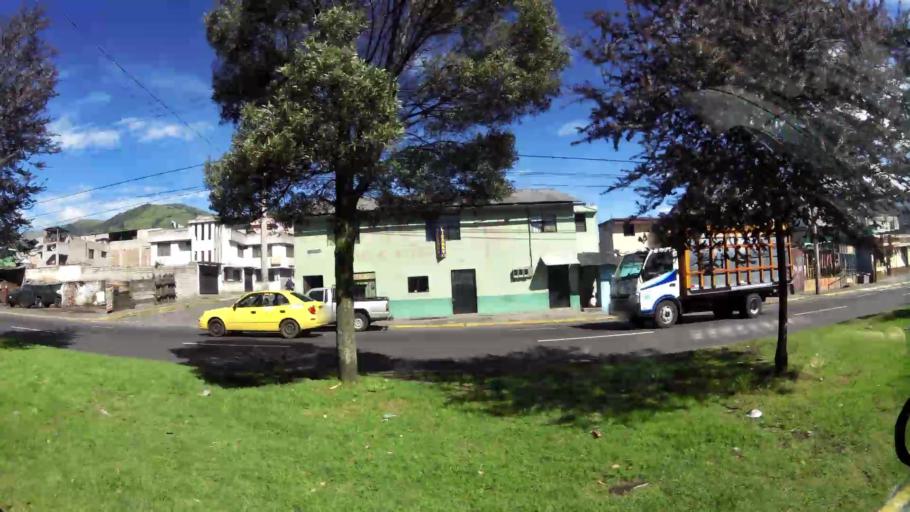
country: EC
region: Pichincha
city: Quito
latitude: -0.3028
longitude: -78.5590
